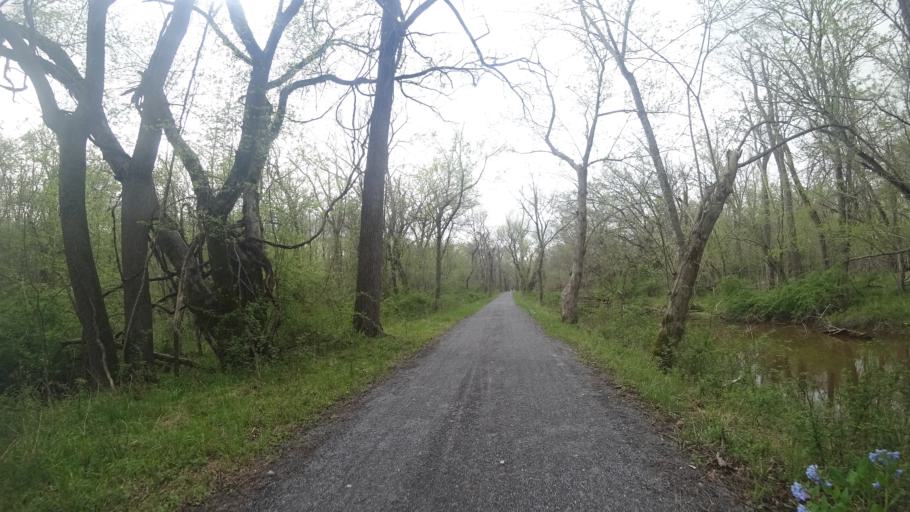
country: US
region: Virginia
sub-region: Loudoun County
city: Belmont
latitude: 39.1194
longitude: -77.4988
